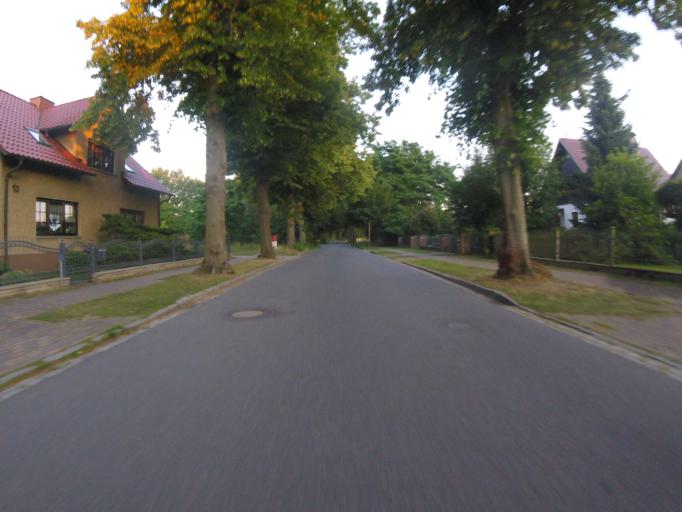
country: DE
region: Brandenburg
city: Konigs Wusterhausen
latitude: 52.2763
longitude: 13.5992
